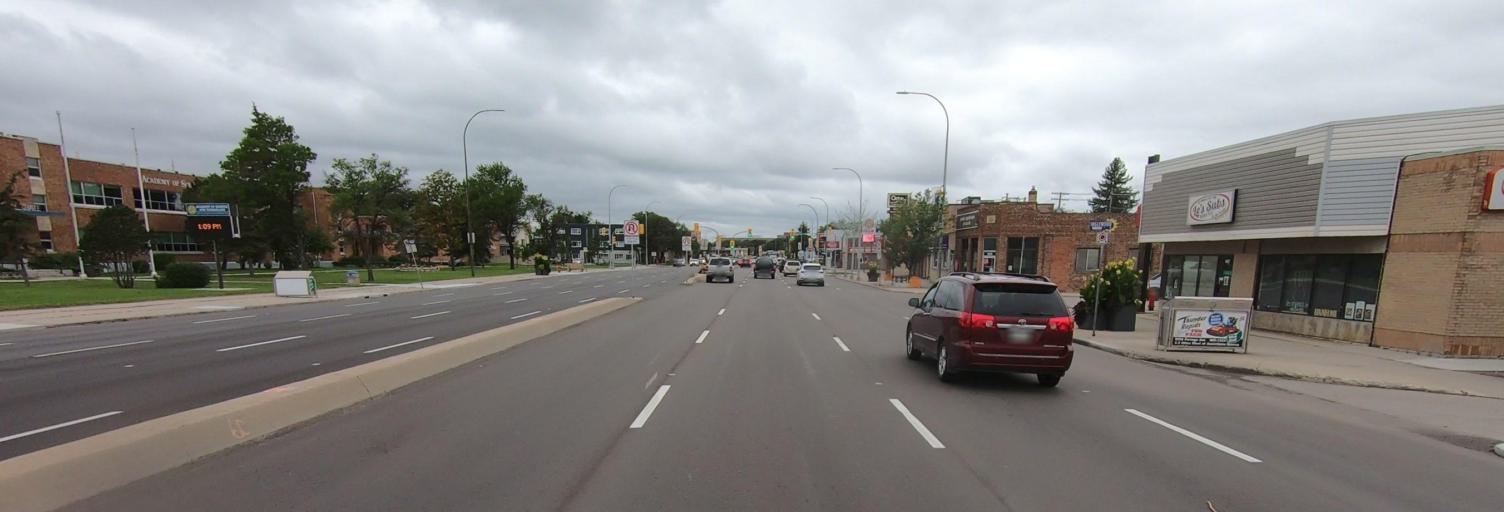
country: CA
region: Manitoba
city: Winnipeg
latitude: 49.8787
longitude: -97.2196
